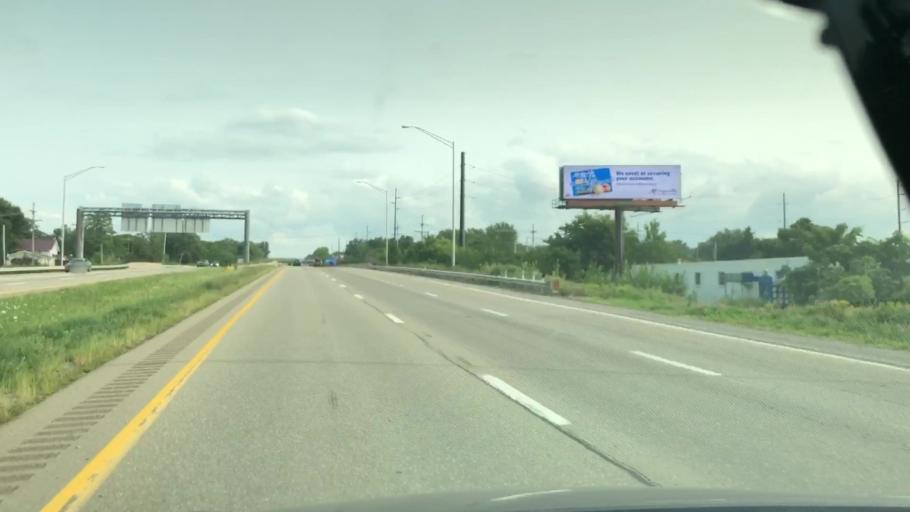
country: US
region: Pennsylvania
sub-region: Erie County
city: Erie
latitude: 42.0906
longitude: -80.1196
